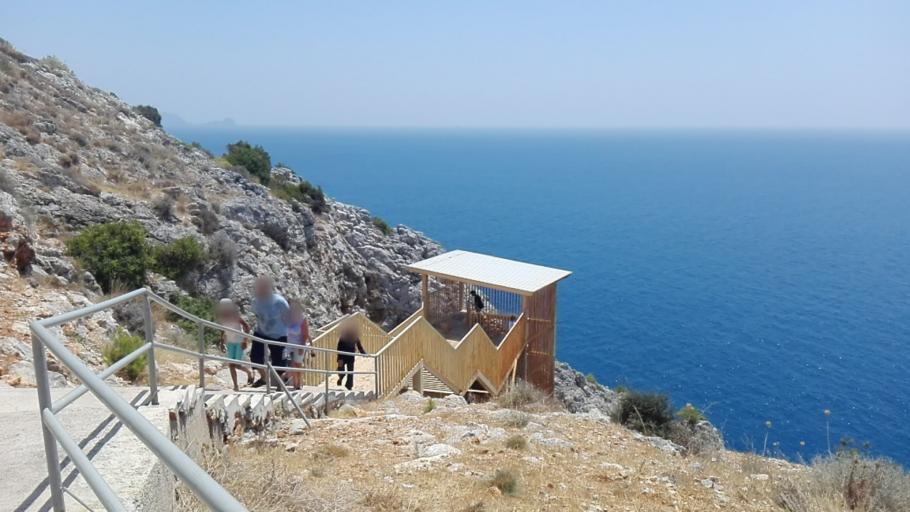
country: TR
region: Mersin
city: Aydincik
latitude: 36.1311
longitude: 33.4023
